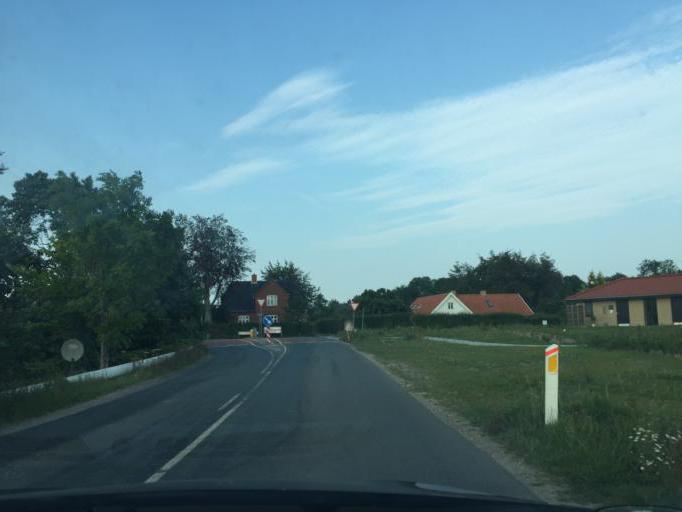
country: DK
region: South Denmark
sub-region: Kerteminde Kommune
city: Langeskov
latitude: 55.3072
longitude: 10.5852
